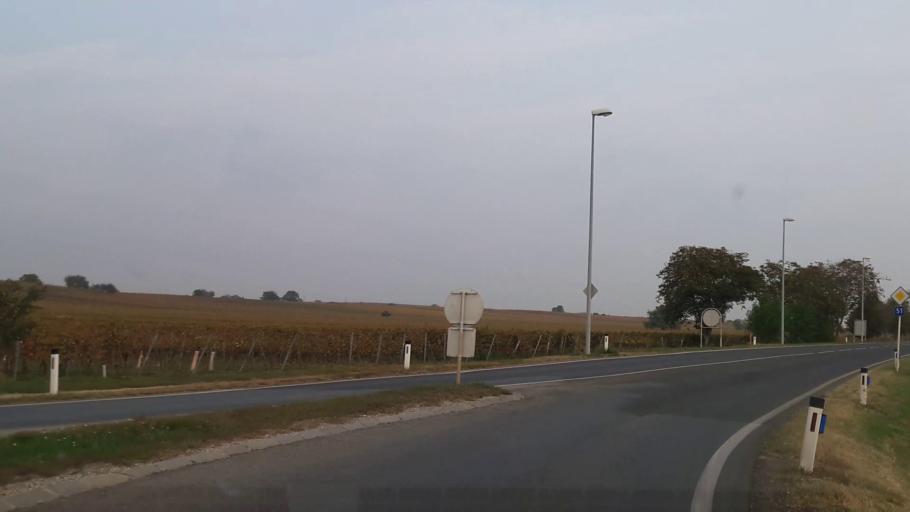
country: AT
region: Burgenland
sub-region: Politischer Bezirk Neusiedl am See
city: Weiden am See
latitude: 47.9118
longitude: 16.8887
